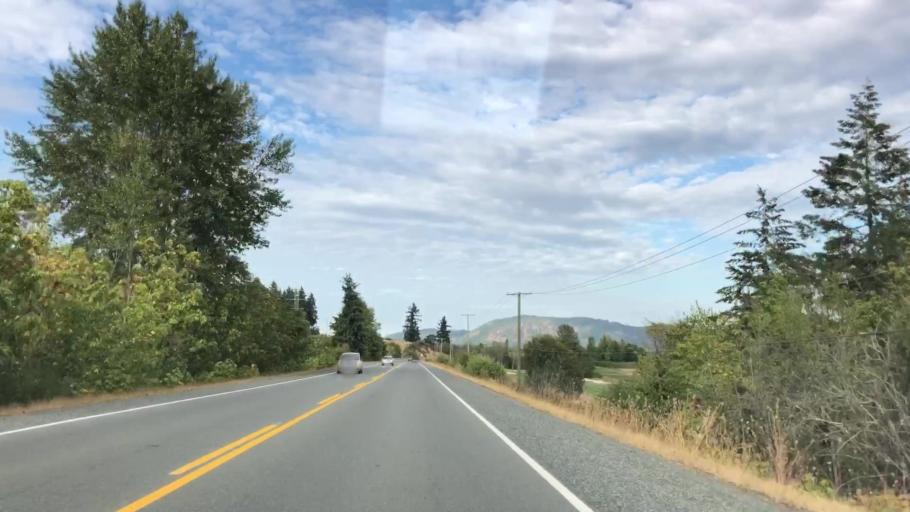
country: CA
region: British Columbia
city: Duncan
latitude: 48.8094
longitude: -123.7517
